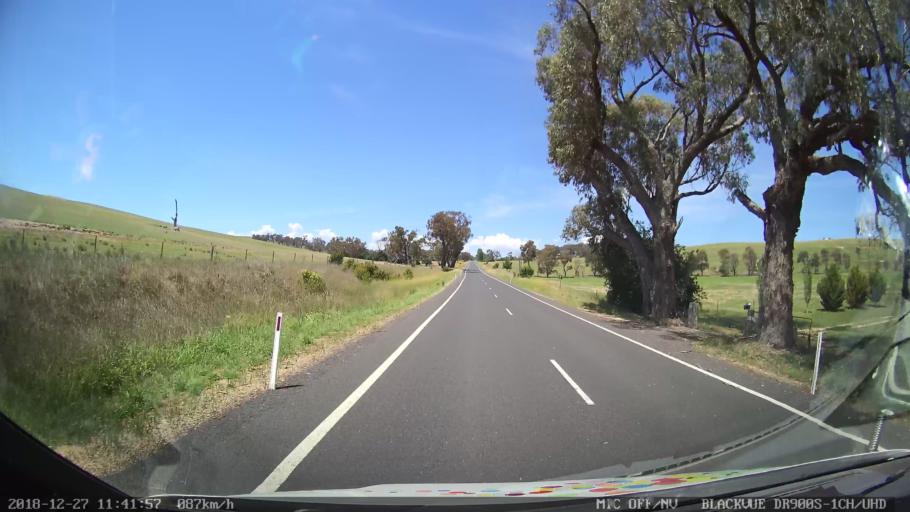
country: AU
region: New South Wales
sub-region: Bathurst Regional
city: Perthville
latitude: -33.5424
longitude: 149.4801
